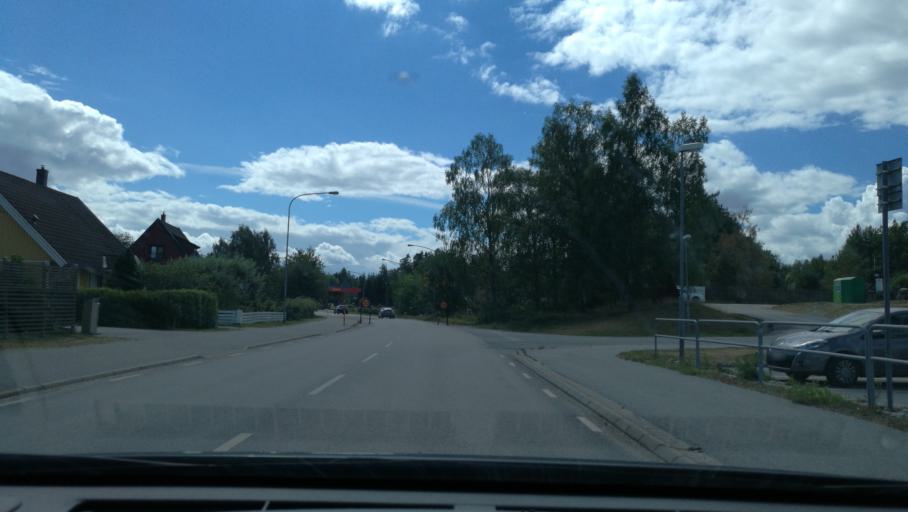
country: SE
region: OEstergoetland
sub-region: Norrkopings Kommun
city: Krokek
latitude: 58.6731
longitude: 16.3639
